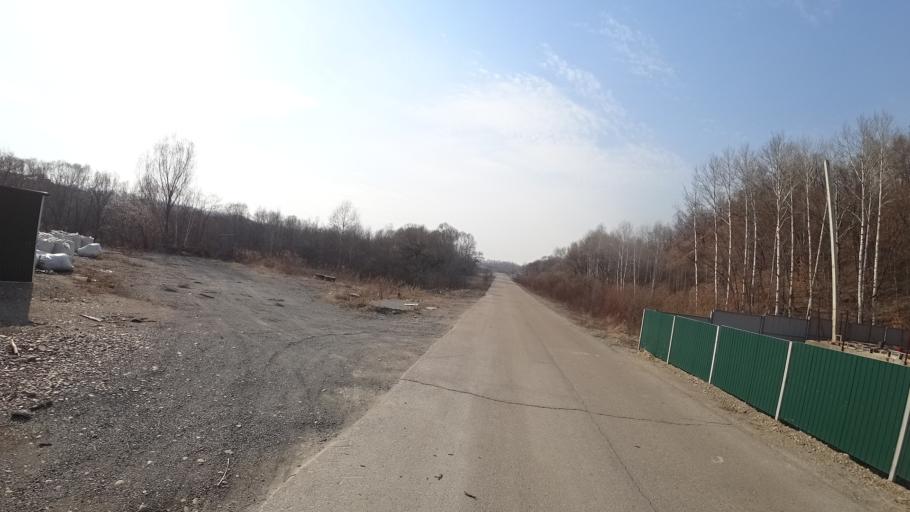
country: RU
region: Amur
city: Novobureyskiy
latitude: 49.7953
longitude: 129.9598
